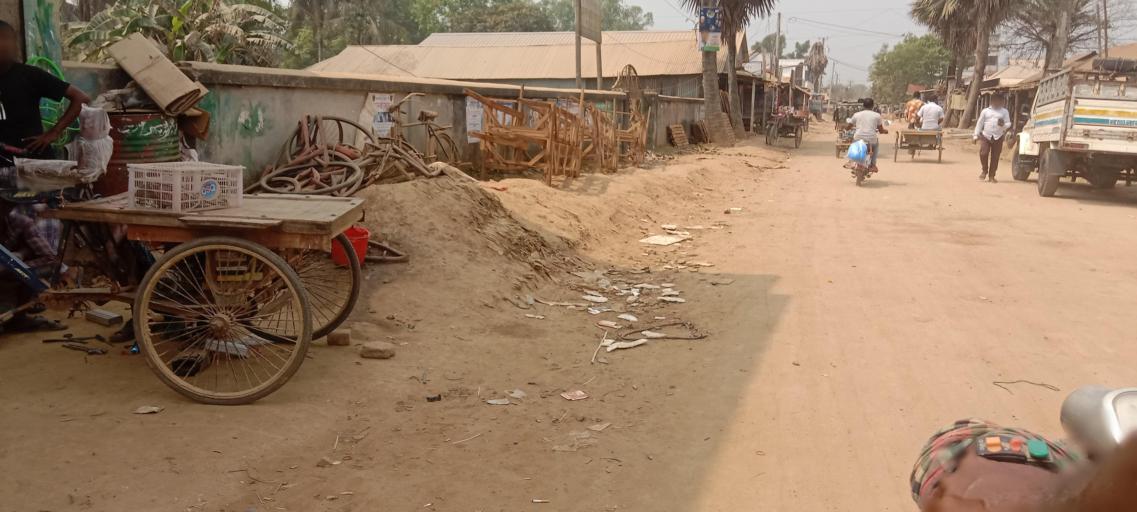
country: BD
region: Dhaka
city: Sakhipur
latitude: 24.3083
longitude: 90.2670
